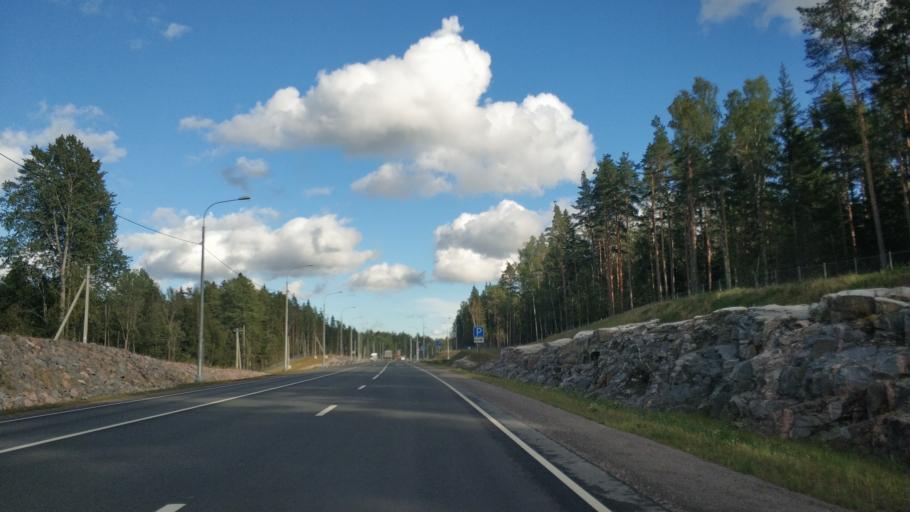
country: RU
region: Leningrad
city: Kuznechnoye
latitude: 61.0952
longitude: 29.9853
